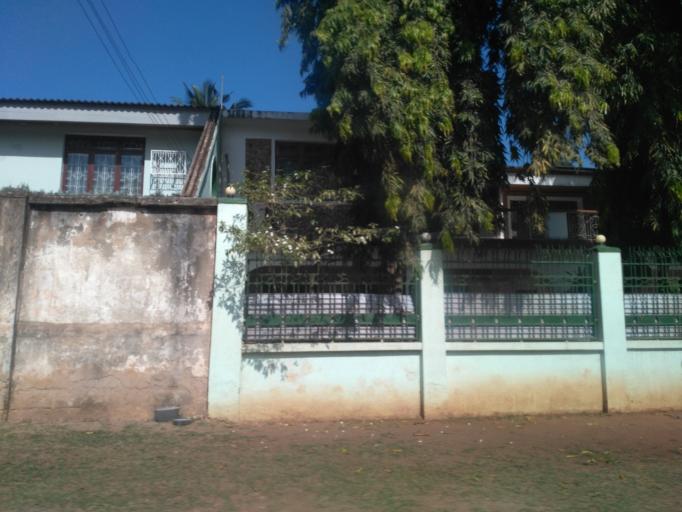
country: TZ
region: Dar es Salaam
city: Magomeni
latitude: -6.7788
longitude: 39.2682
